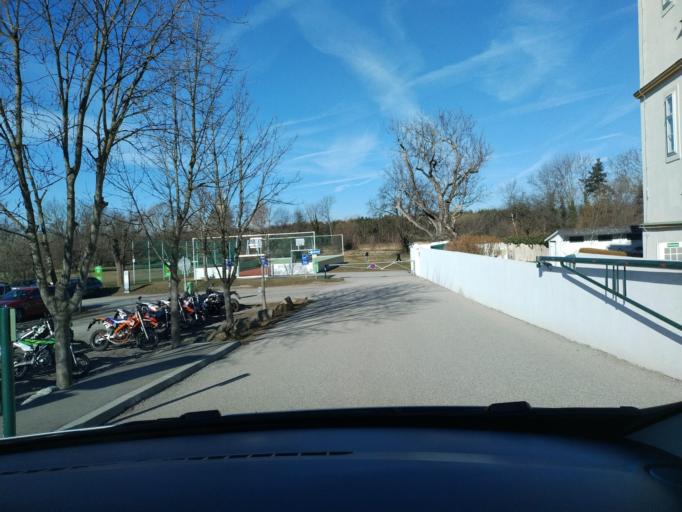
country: AT
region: Lower Austria
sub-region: Politischer Bezirk Wiener Neustadt
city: Lanzenkirchen
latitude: 47.7423
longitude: 16.2511
